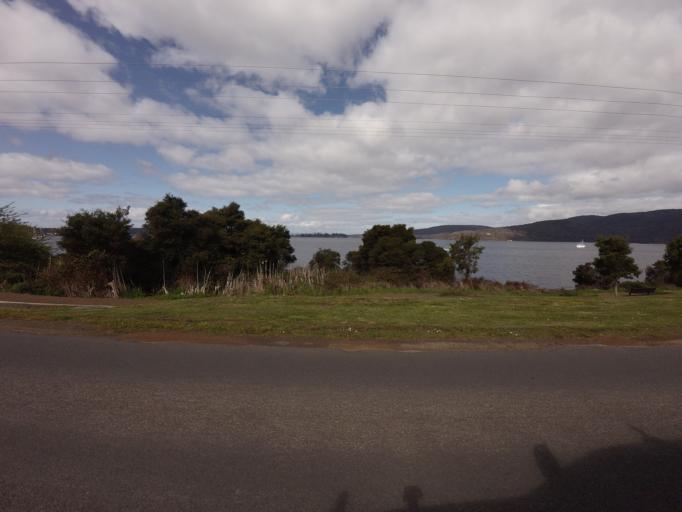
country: AU
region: Tasmania
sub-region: Huon Valley
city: Geeveston
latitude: -43.3184
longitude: 147.0096
